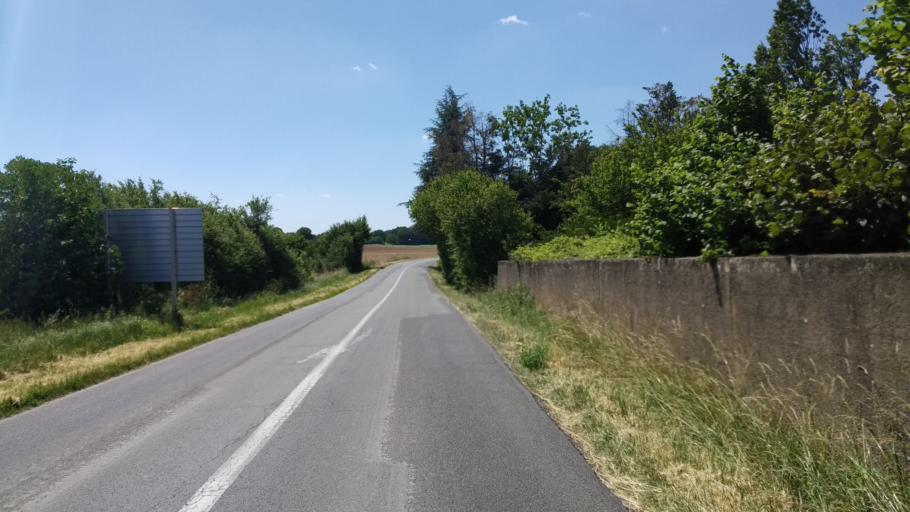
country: FR
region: Poitou-Charentes
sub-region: Departement de la Vienne
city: Biard
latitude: 46.5985
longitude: 0.3008
